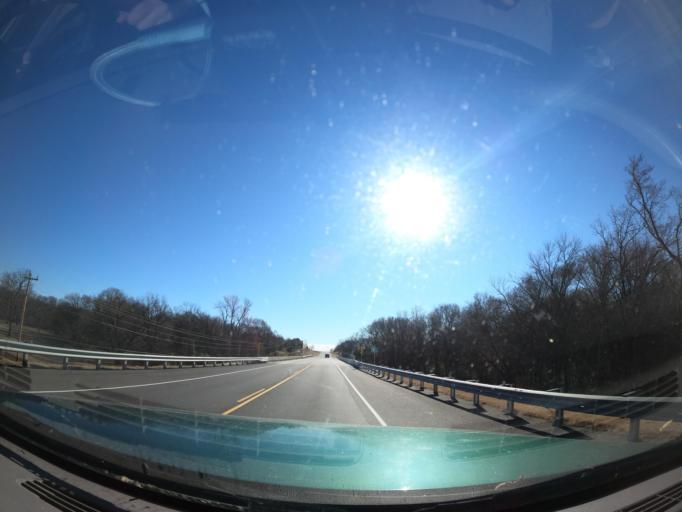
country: US
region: Oklahoma
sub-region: Muskogee County
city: Haskell
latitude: 35.8435
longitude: -95.6776
